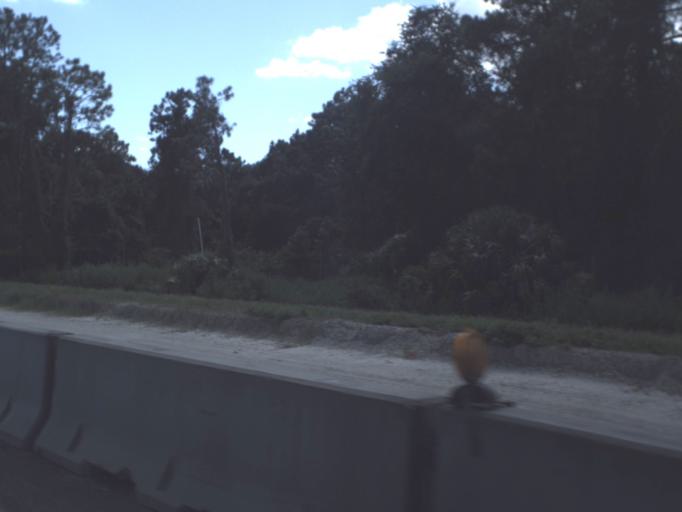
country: US
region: Florida
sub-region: Pasco County
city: Wesley Chapel
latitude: 28.2879
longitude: -82.3262
